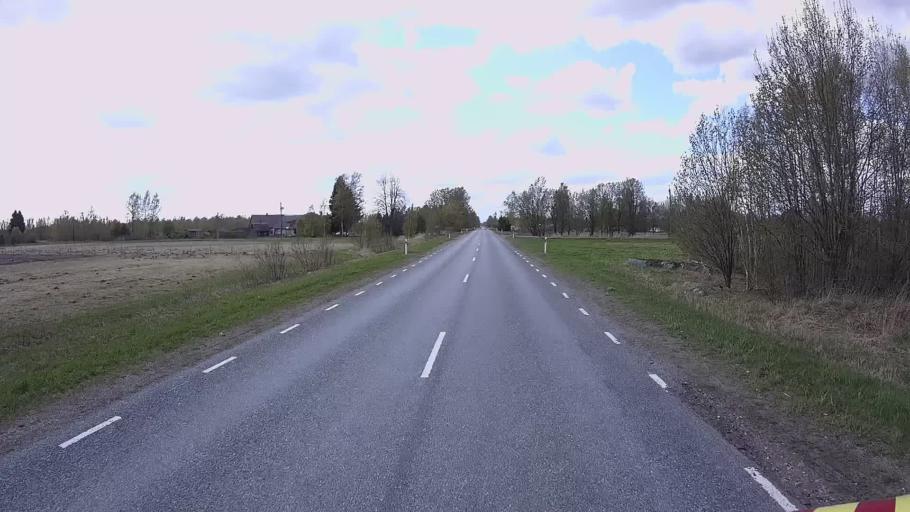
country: EE
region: Jogevamaa
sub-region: Mustvee linn
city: Mustvee
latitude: 58.7852
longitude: 26.9674
